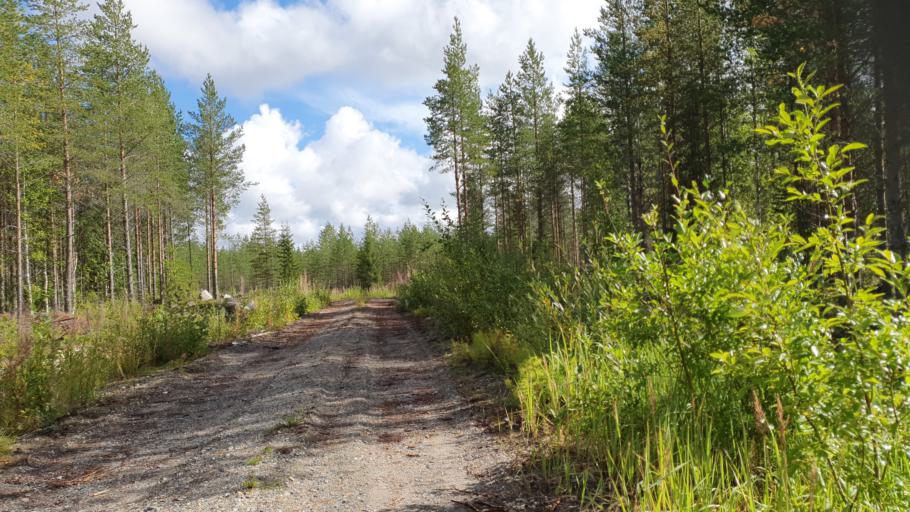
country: FI
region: Kainuu
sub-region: Kehys-Kainuu
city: Kuhmo
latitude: 64.1394
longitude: 29.3926
